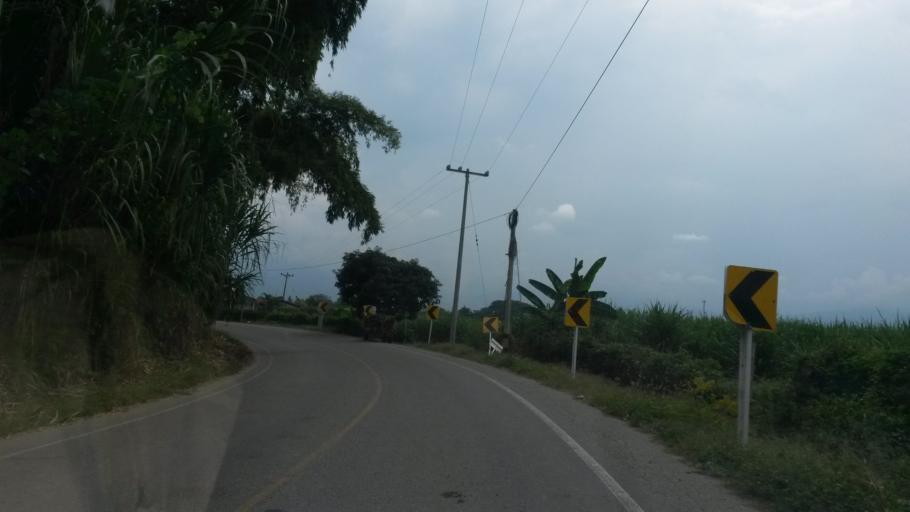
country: CO
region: Cauca
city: Padilla
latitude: 3.2277
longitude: -76.3184
